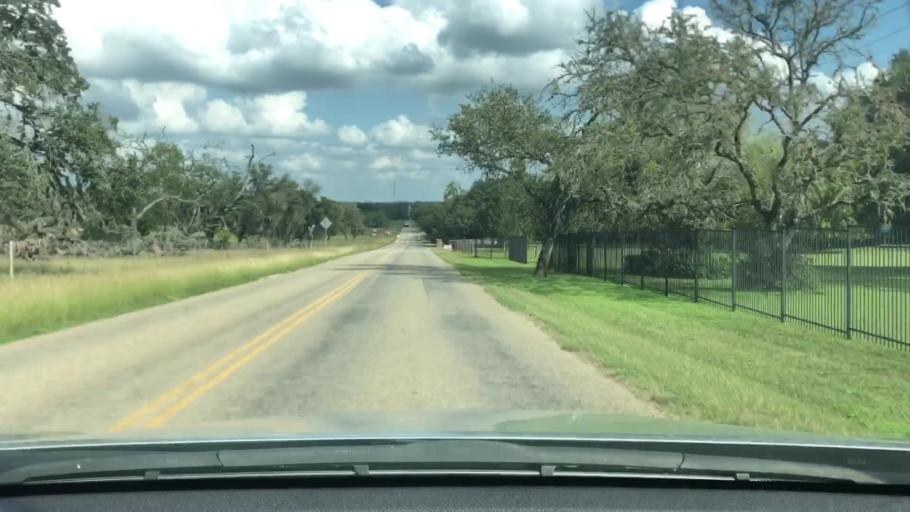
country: US
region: Texas
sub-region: Bexar County
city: Fair Oaks Ranch
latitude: 29.7859
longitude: -98.6602
